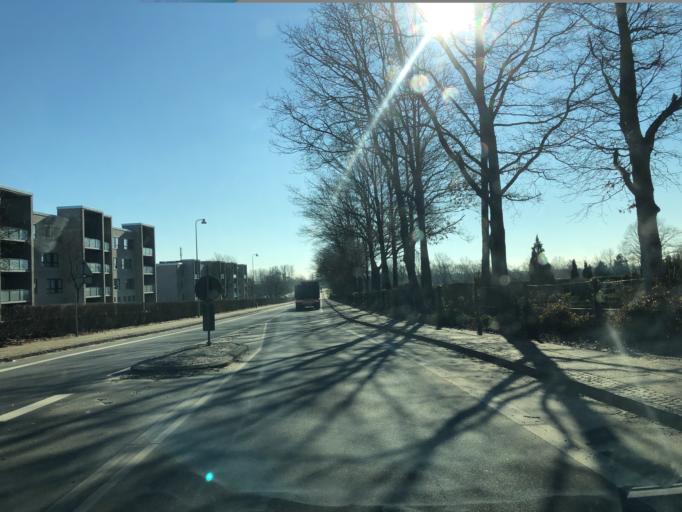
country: DK
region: Central Jutland
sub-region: Ikast-Brande Kommune
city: Ikast
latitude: 56.1369
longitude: 9.1648
